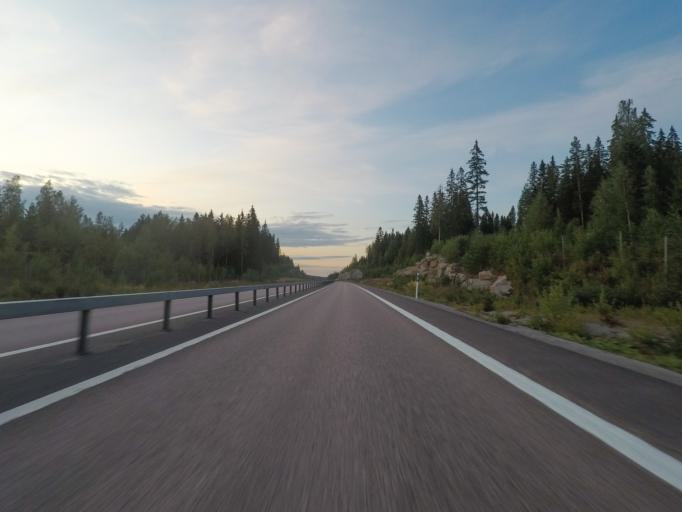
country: FI
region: Central Finland
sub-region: Jyvaeskylae
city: Saeynaetsalo
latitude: 62.1788
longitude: 25.9066
